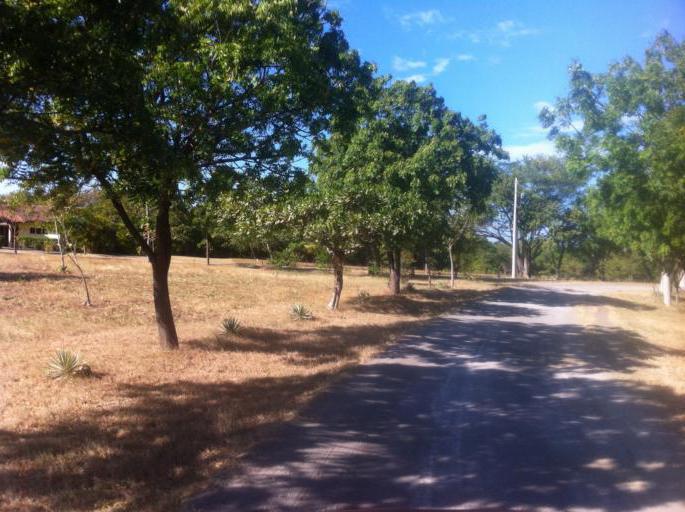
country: NI
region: Managua
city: Carlos Fonseca Amador
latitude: 11.9037
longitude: -86.6086
